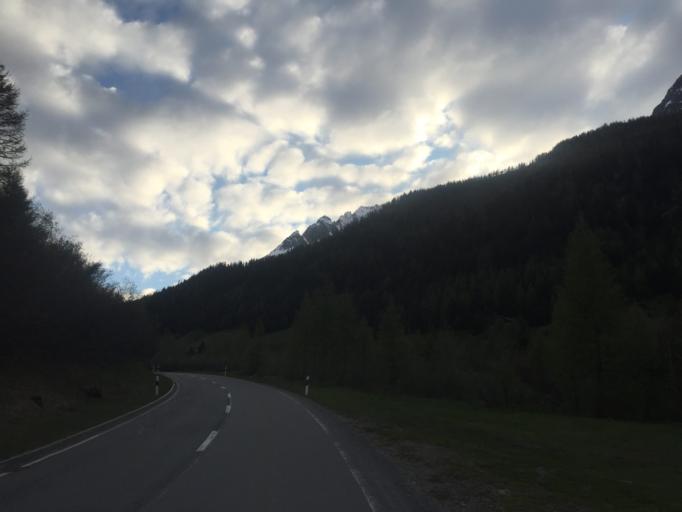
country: CH
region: Ticino
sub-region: Leventina District
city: Airolo
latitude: 46.4974
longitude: 8.4993
